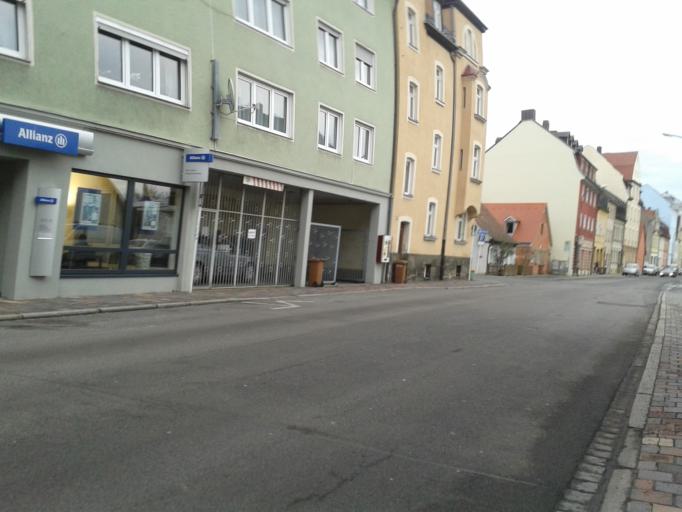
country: DE
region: Bavaria
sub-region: Upper Franconia
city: Bamberg
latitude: 49.8946
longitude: 10.9041
